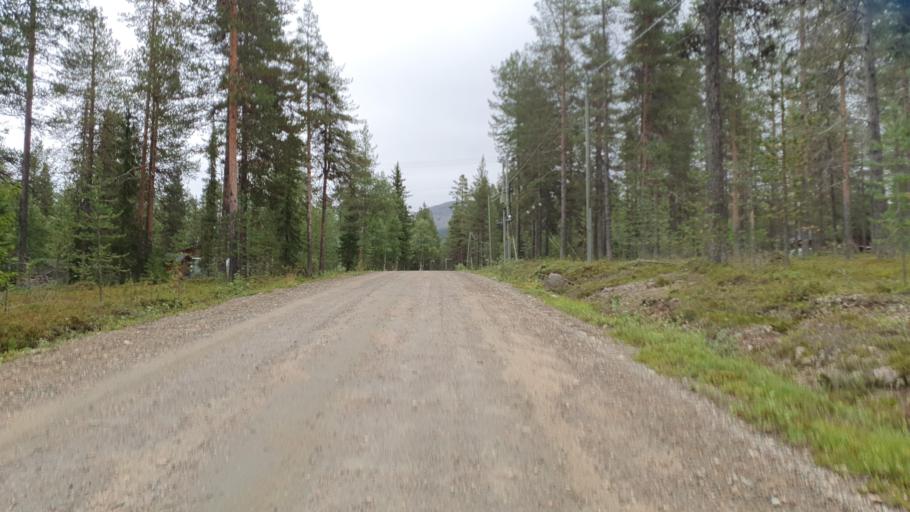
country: FI
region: Lapland
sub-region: Tunturi-Lappi
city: Kolari
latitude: 67.6012
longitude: 24.1894
